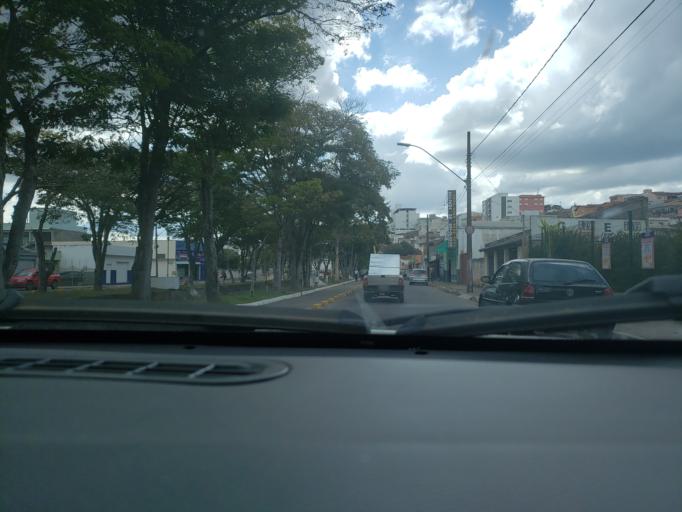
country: BR
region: Minas Gerais
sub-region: Campo Belo
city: Campo Belo
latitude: -20.8970
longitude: -45.2675
